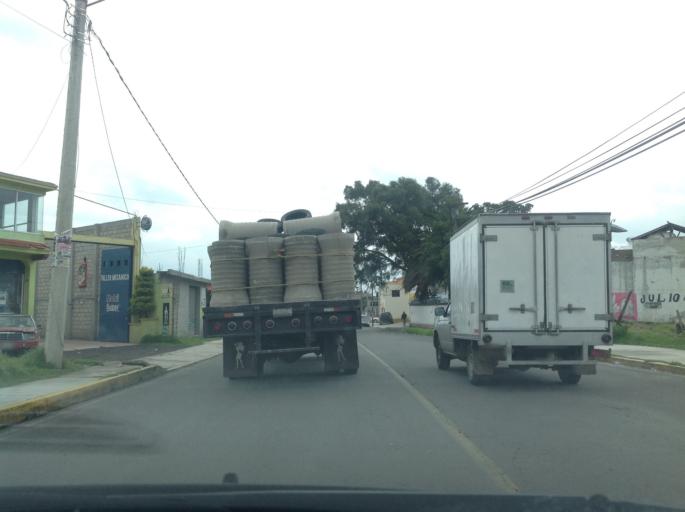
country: MX
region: Morelos
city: Tenango de Arista
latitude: 19.1036
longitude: -99.5829
